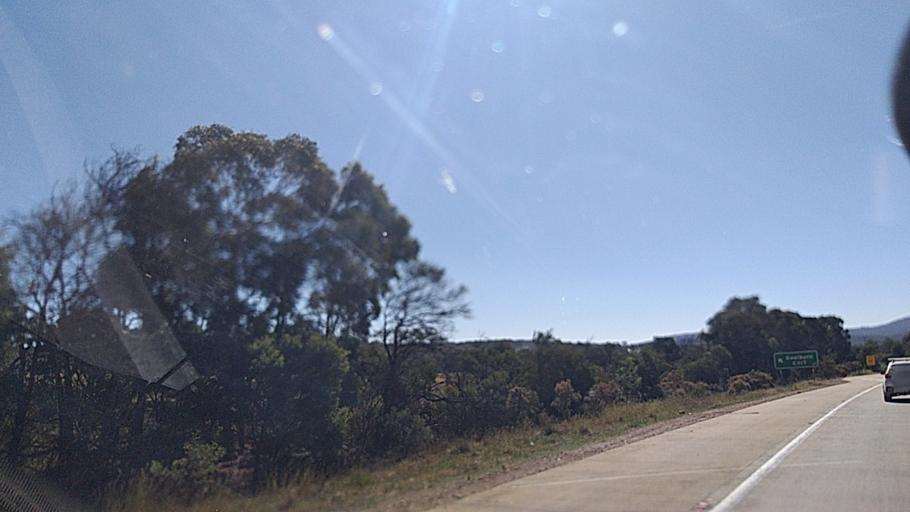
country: AU
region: New South Wales
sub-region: Goulburn Mulwaree
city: Goulburn
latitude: -34.7472
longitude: 149.7693
